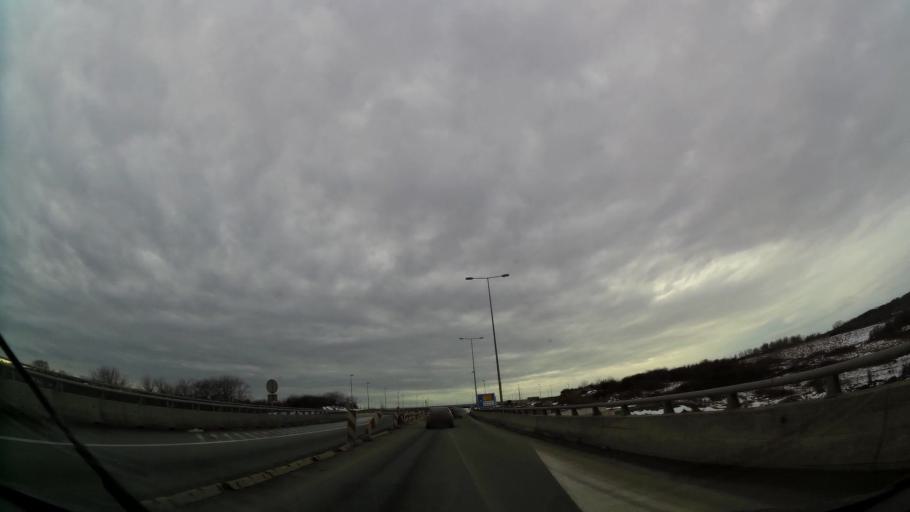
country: RS
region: Central Serbia
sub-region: Belgrade
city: Rakovica
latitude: 44.7127
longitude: 20.4212
